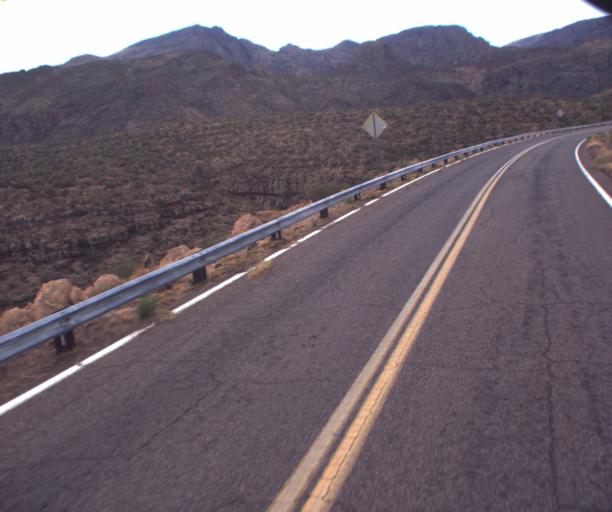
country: US
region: Arizona
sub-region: Pinal County
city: Apache Junction
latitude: 33.5363
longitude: -111.3467
